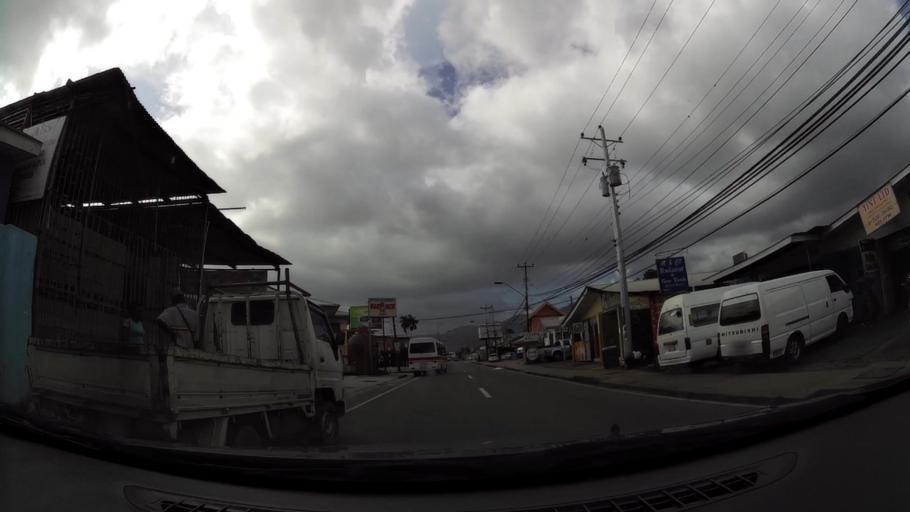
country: TT
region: Tunapuna/Piarco
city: Arouca
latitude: 10.6384
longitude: -61.3480
